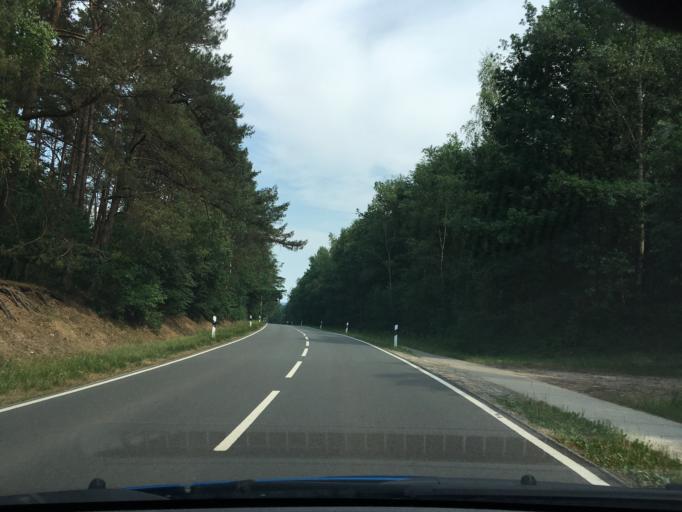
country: DE
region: Lower Saxony
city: Asendorf
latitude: 53.2670
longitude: 9.9633
